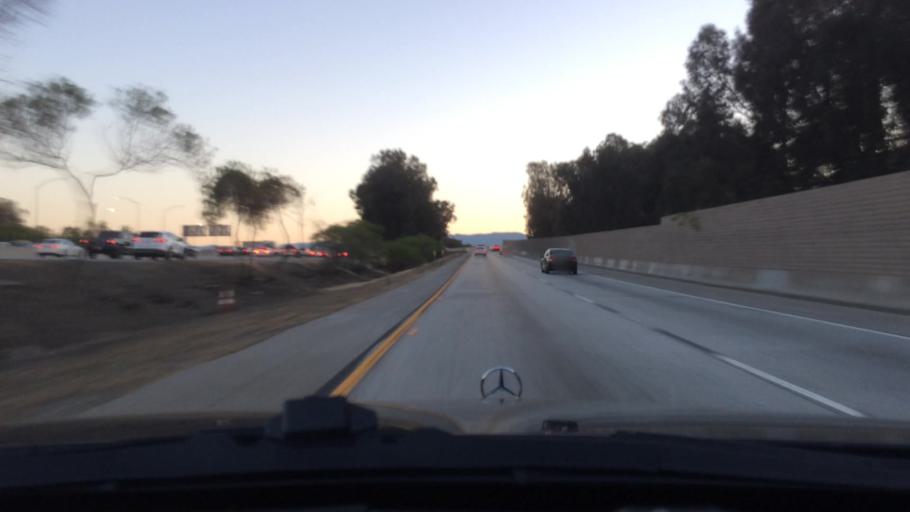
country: US
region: California
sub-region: Los Angeles County
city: Norwalk
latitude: 33.9075
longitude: -118.1047
